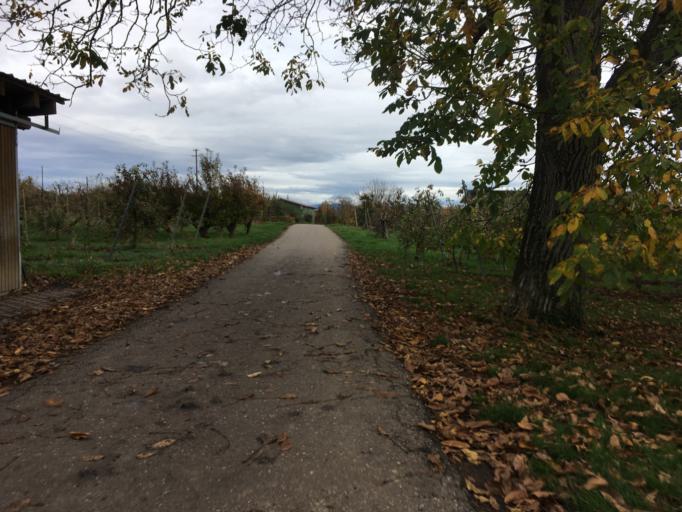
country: DE
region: Baden-Wuerttemberg
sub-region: Freiburg Region
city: Ihringen
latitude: 48.0420
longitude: 7.6338
